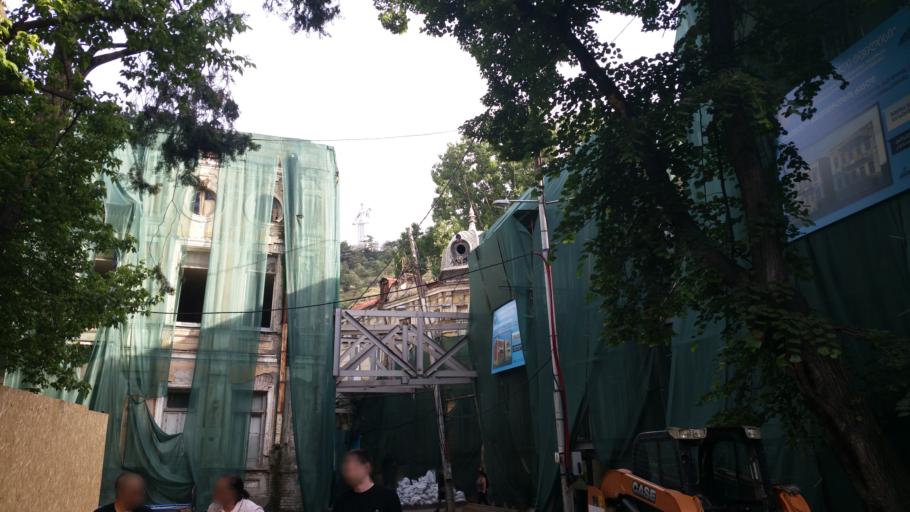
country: GE
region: T'bilisi
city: Tbilisi
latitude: 41.6909
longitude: 44.8035
